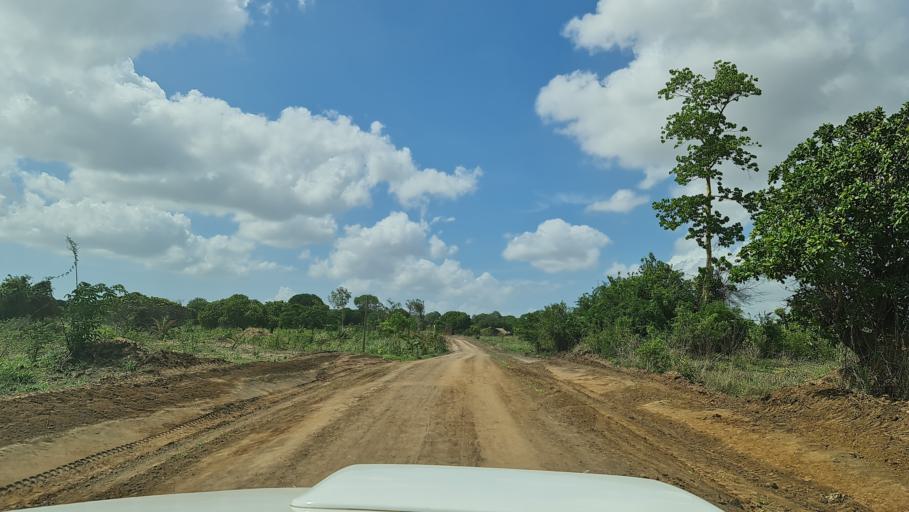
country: MZ
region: Nampula
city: Ilha de Mocambique
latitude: -15.0136
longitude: 40.5603
